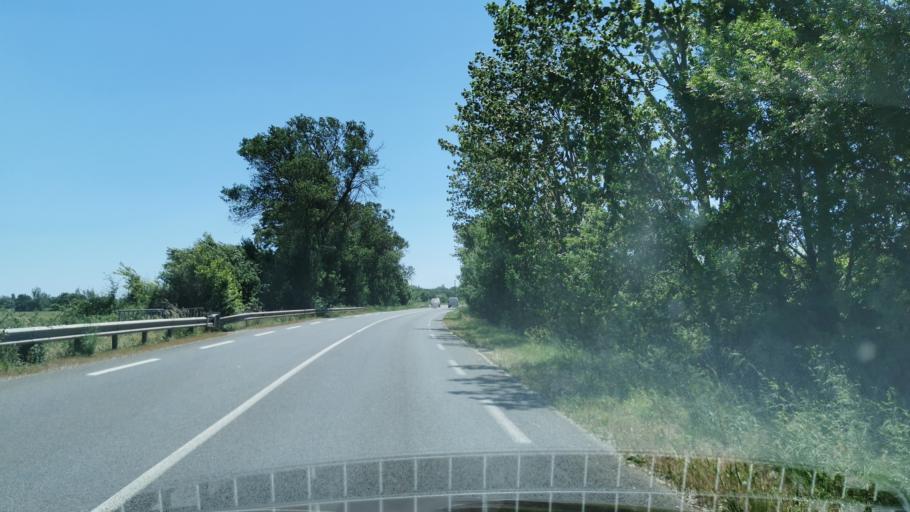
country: FR
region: Languedoc-Roussillon
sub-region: Departement de l'Aude
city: Narbonne
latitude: 43.2176
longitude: 3.0113
